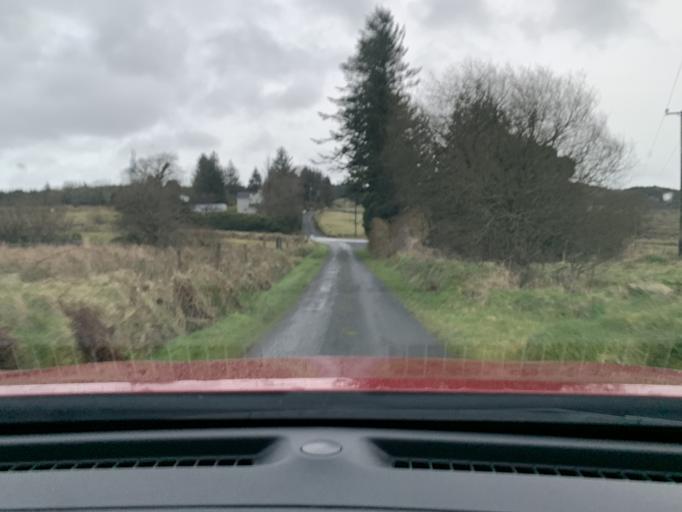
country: IE
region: Connaught
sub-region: Roscommon
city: Boyle
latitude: 53.9974
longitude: -8.3092
